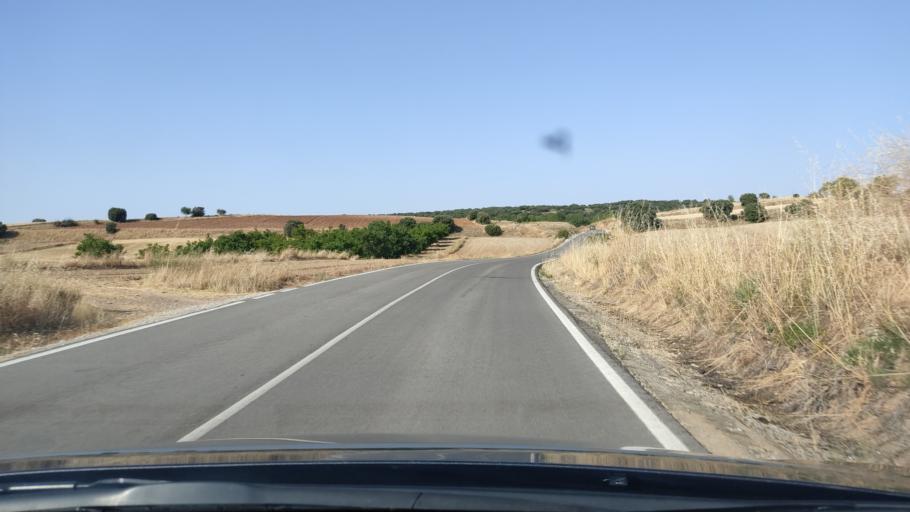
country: ES
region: Aragon
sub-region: Provincia de Teruel
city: Cucalon
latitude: 41.0774
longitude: -1.2257
